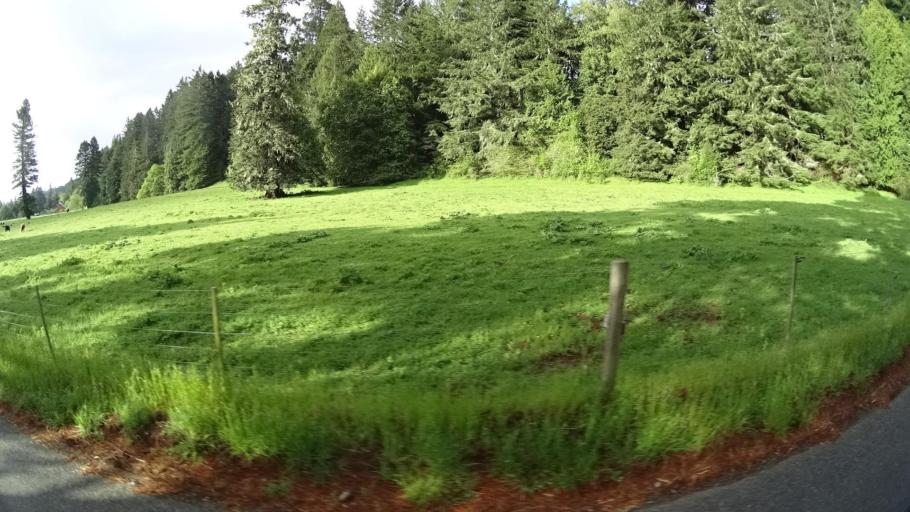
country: US
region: California
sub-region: Humboldt County
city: Blue Lake
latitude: 40.8744
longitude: -124.0083
